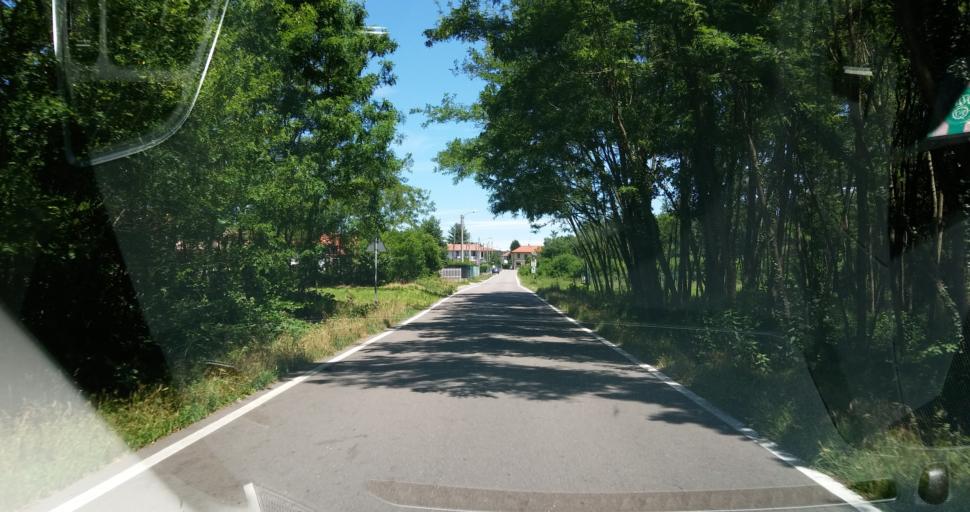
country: IT
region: Lombardy
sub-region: Provincia di Varese
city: Cimbro
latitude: 45.7444
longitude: 8.7238
